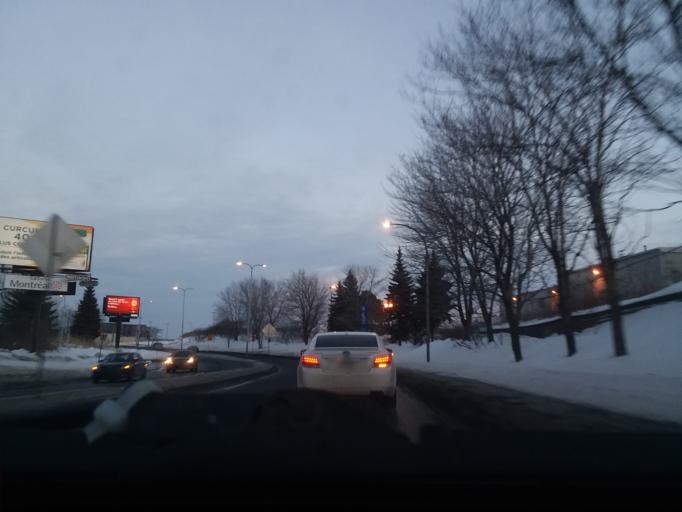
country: CA
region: Quebec
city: Saint-Raymond
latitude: 45.4501
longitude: -73.6230
